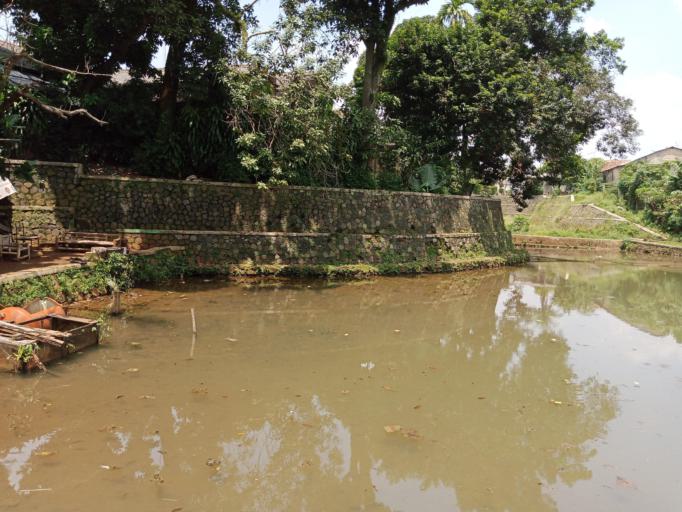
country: ID
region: West Java
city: Depok
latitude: -6.4044
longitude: 106.8101
